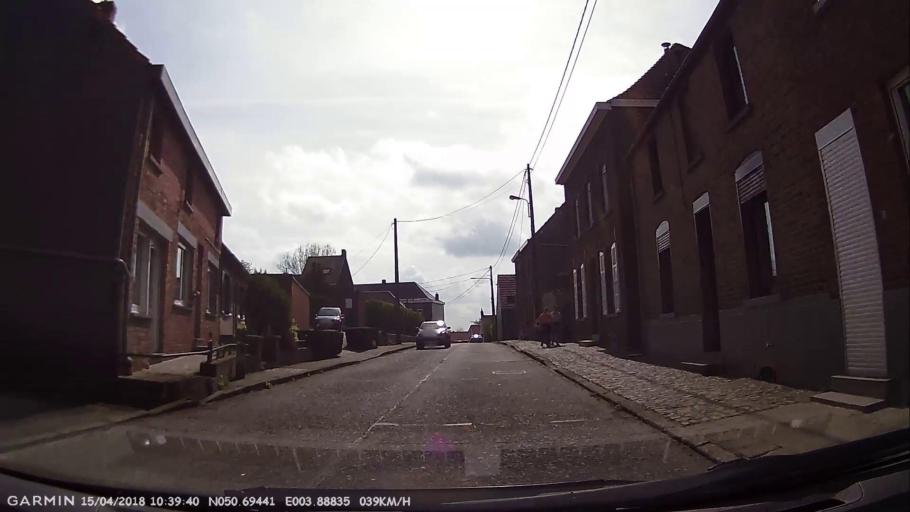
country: BE
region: Wallonia
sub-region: Province du Hainaut
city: Lessines
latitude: 50.6943
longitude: 3.8884
